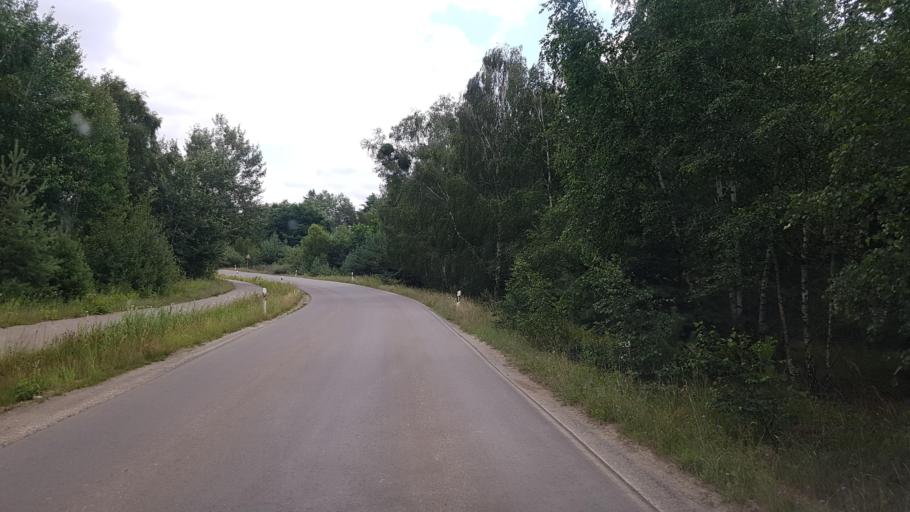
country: DE
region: Brandenburg
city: Altdobern
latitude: 51.6423
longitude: 14.0961
